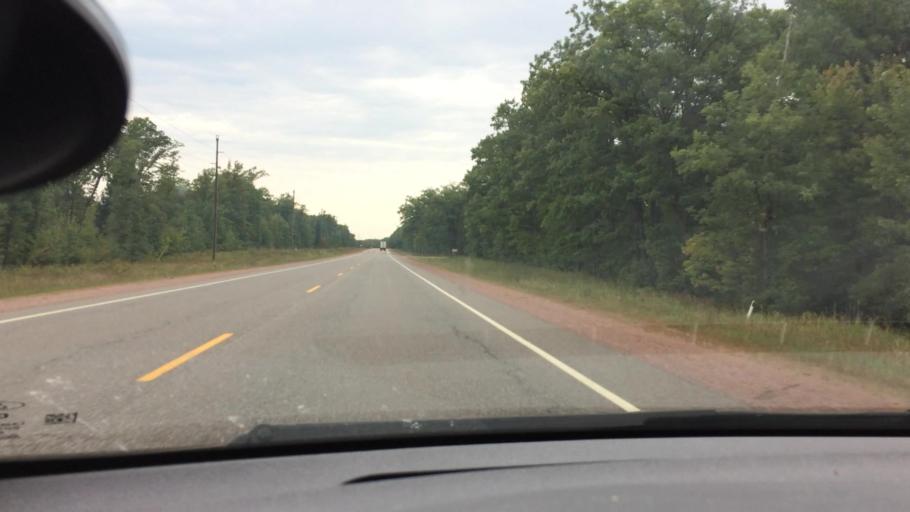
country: US
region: Wisconsin
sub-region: Clark County
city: Neillsville
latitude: 44.5769
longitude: -90.7359
